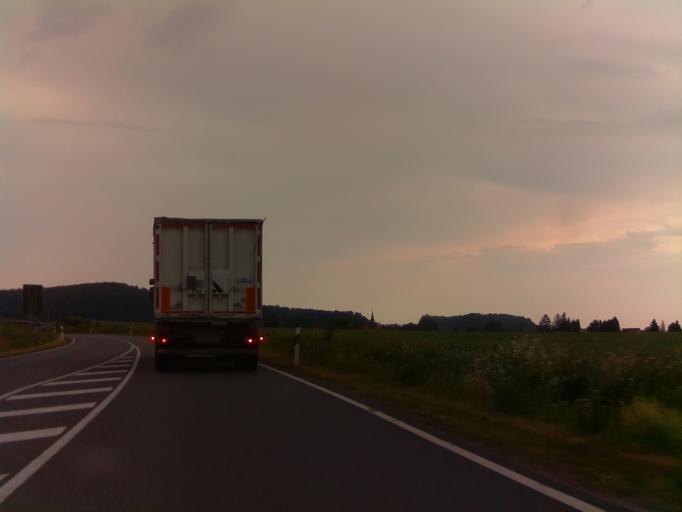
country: DE
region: Lower Saxony
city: Heinsen
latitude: 52.1098
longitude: 9.6824
